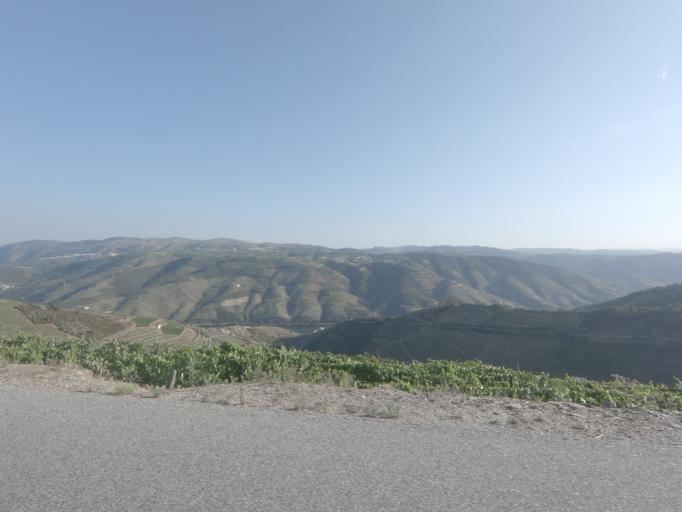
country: PT
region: Vila Real
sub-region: Sabrosa
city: Vilela
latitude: 41.1743
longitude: -7.5968
